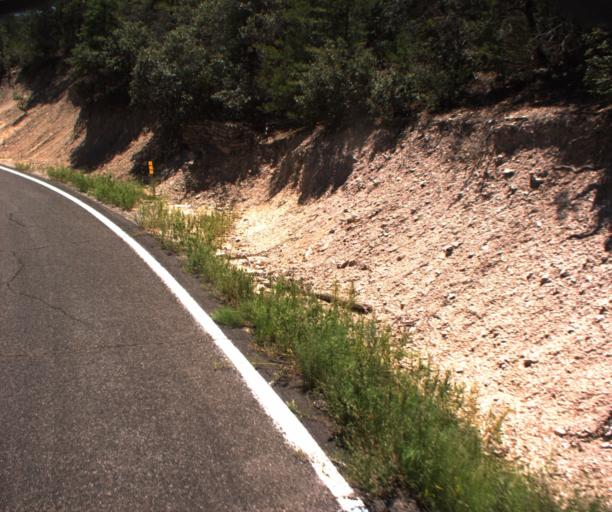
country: US
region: Arizona
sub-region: Greenlee County
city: Morenci
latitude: 33.1909
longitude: -109.3848
